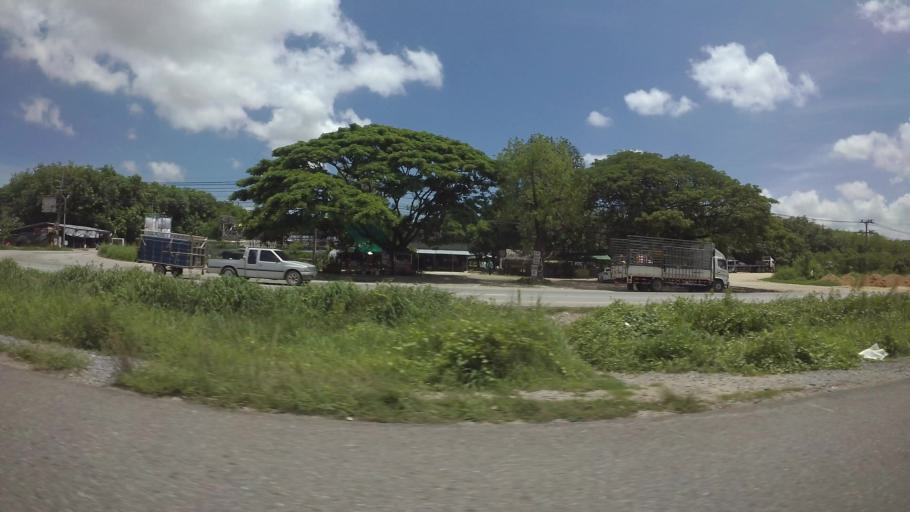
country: TH
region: Rayong
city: Nikhom Phattana
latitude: 12.7621
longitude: 101.1828
